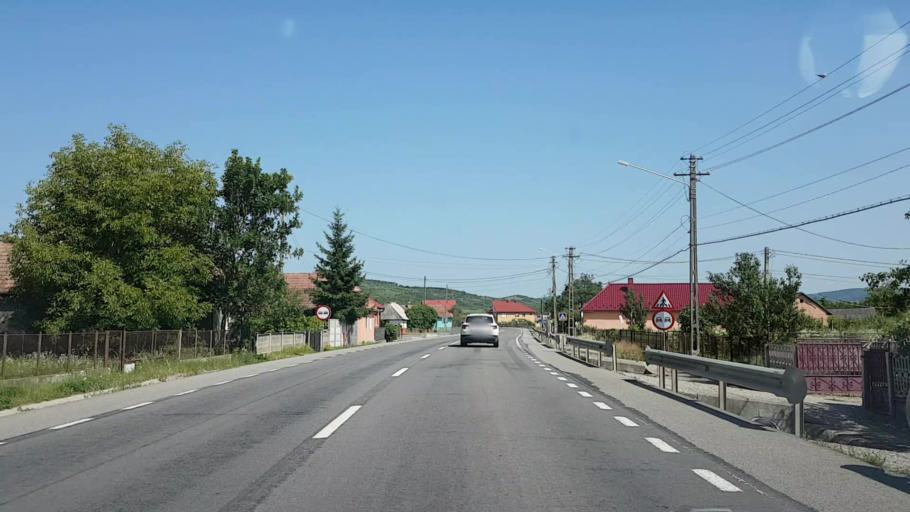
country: RO
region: Bistrita-Nasaud
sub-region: Comuna Sintereag
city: Sintereag
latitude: 47.1794
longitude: 24.2932
